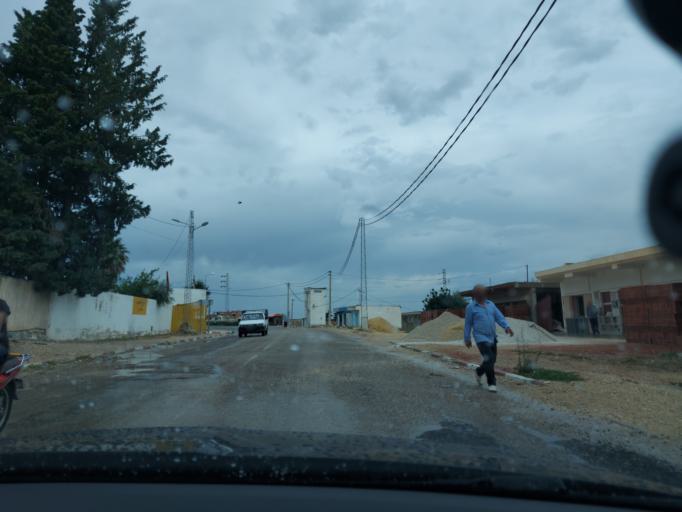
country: TN
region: Silyanah
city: Maktar
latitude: 35.8543
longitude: 9.2119
